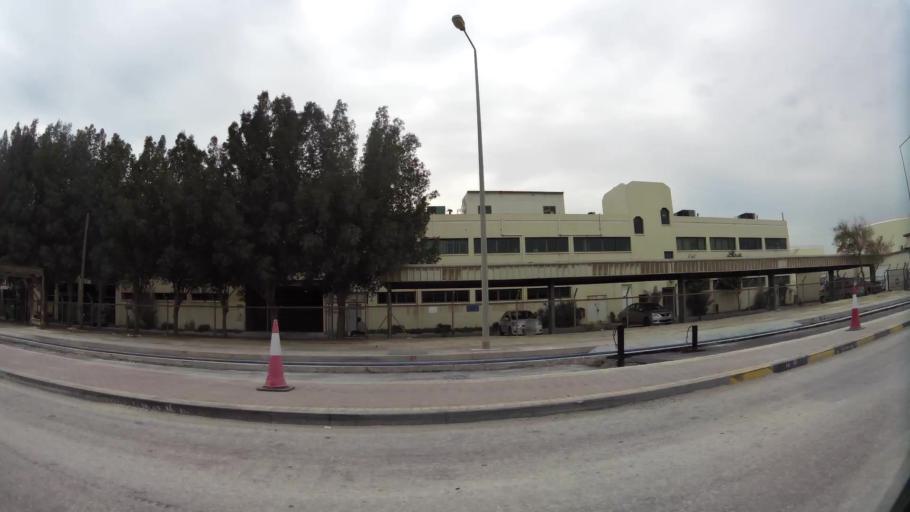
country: BH
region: Northern
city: Sitrah
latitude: 26.1818
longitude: 50.6217
